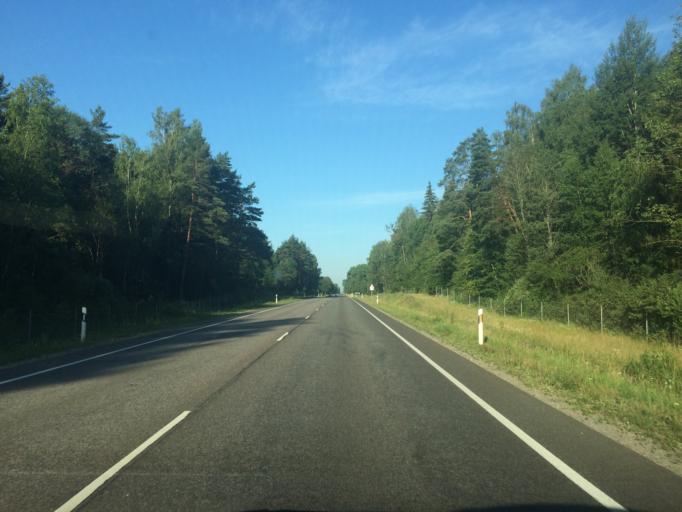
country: LT
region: Vilnius County
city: Ukmerge
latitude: 55.1925
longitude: 24.5961
